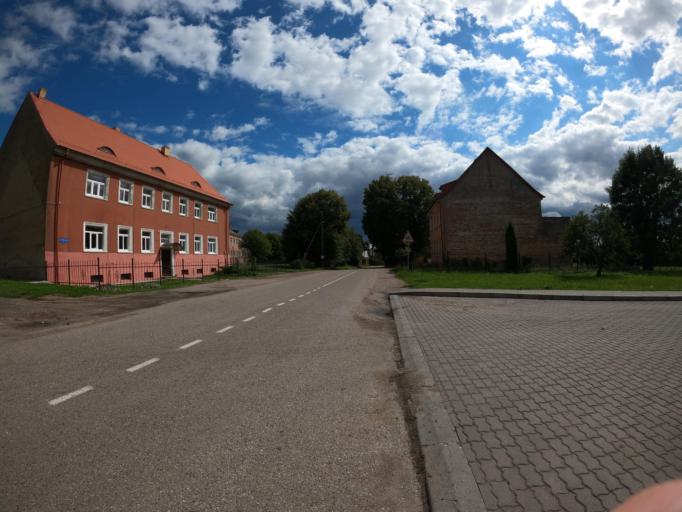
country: RU
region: Kaliningrad
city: Zheleznodorozhnyy
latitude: 54.3634
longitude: 21.3012
